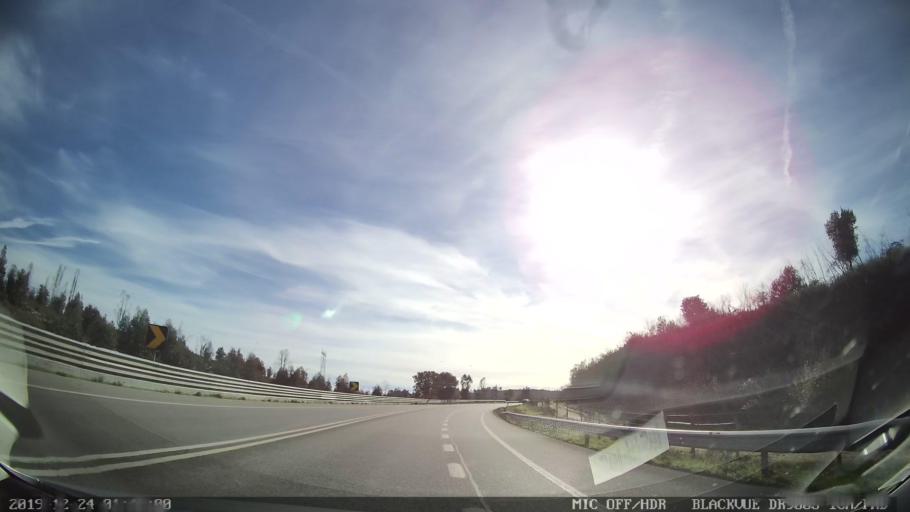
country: PT
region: Portalegre
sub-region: Nisa
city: Nisa
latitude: 39.5151
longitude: -7.7689
